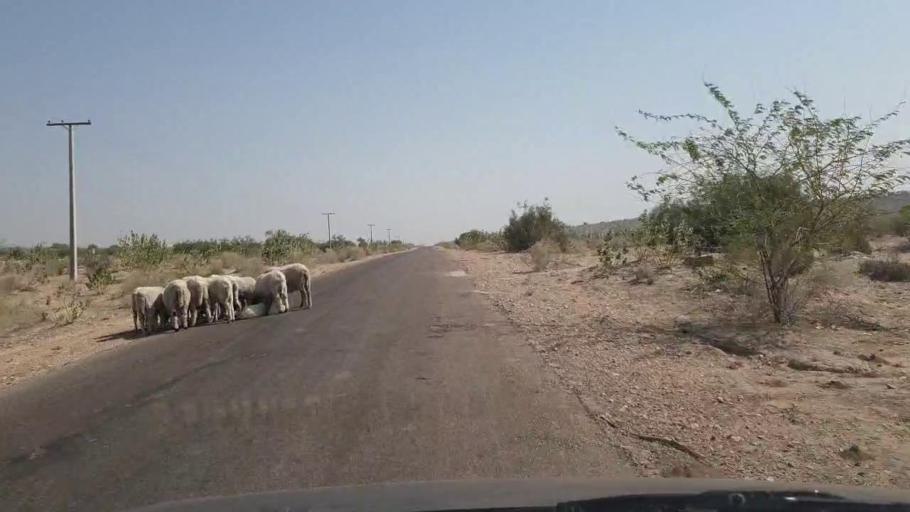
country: PK
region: Sindh
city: Chor
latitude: 25.5745
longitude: 69.9089
